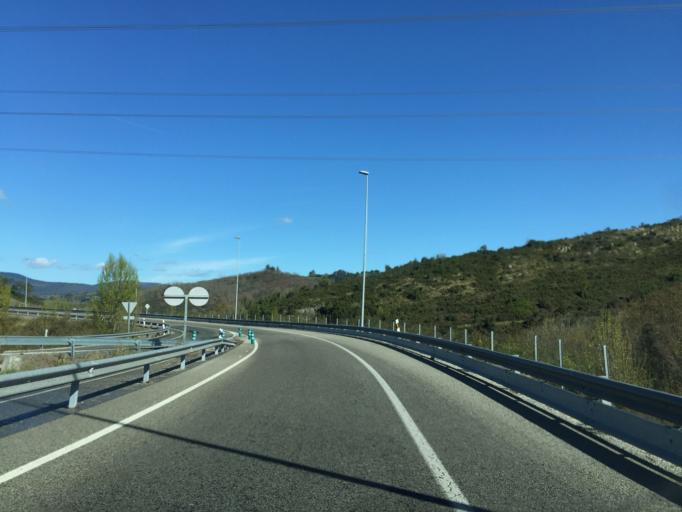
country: ES
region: Asturias
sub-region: Province of Asturias
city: Llanera
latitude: 43.3627
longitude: -5.9481
